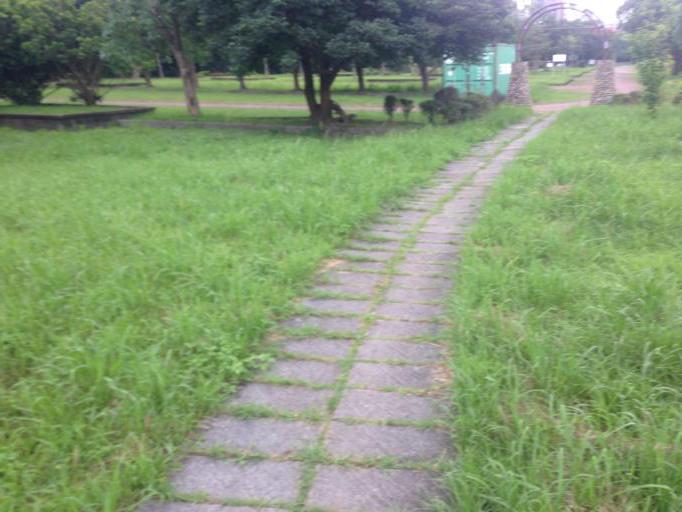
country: TW
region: Taiwan
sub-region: Taoyuan
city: Taoyuan
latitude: 24.9363
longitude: 121.3828
